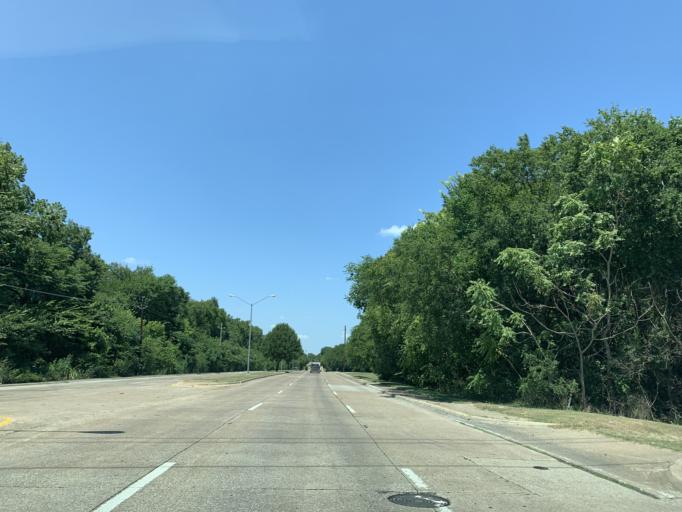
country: US
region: Texas
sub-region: Dallas County
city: Hutchins
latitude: 32.6839
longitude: -96.7681
